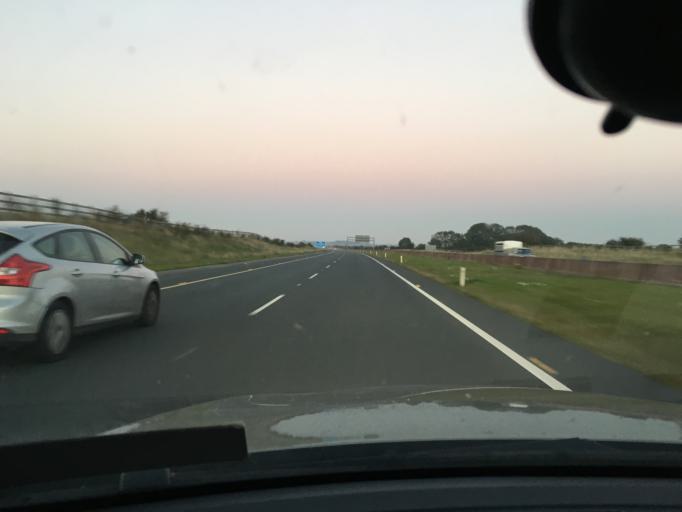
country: IE
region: Connaught
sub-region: County Galway
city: Oranmore
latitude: 53.2962
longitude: -8.9064
